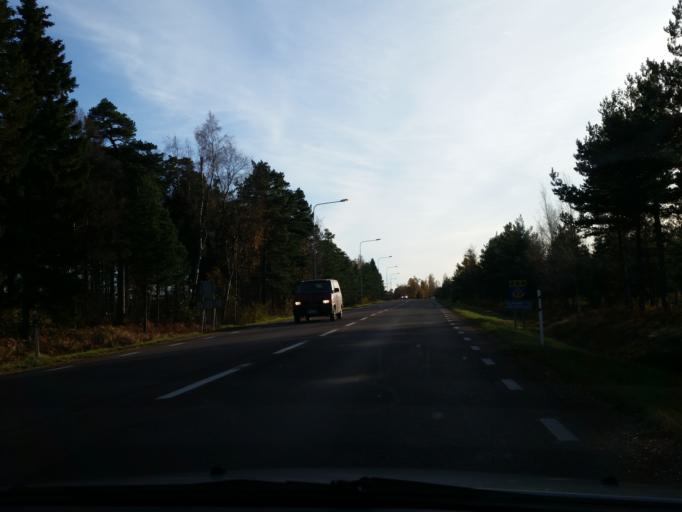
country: AX
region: Alands landsbygd
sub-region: Jomala
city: Jomala
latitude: 60.1275
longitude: 19.9341
